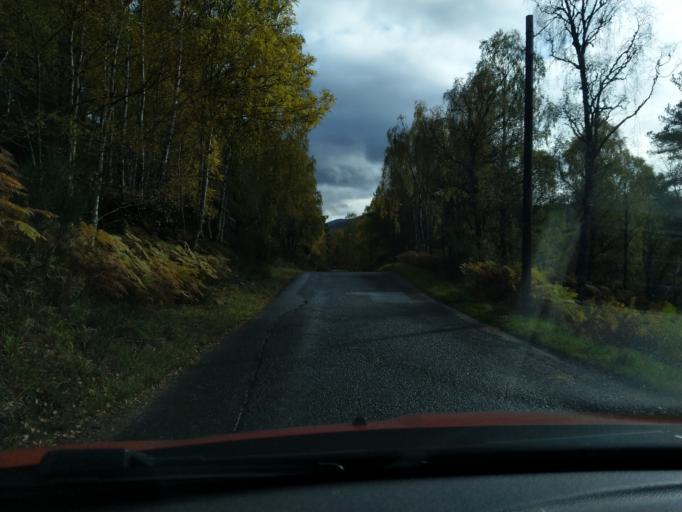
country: GB
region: Scotland
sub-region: Perth and Kinross
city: Aberfeldy
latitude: 56.7089
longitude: -4.0654
